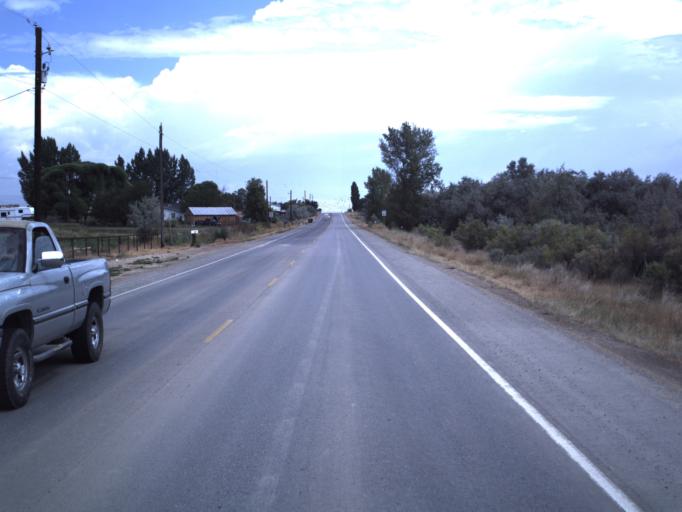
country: US
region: Utah
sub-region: Uintah County
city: Naples
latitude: 40.3728
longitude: -109.4983
